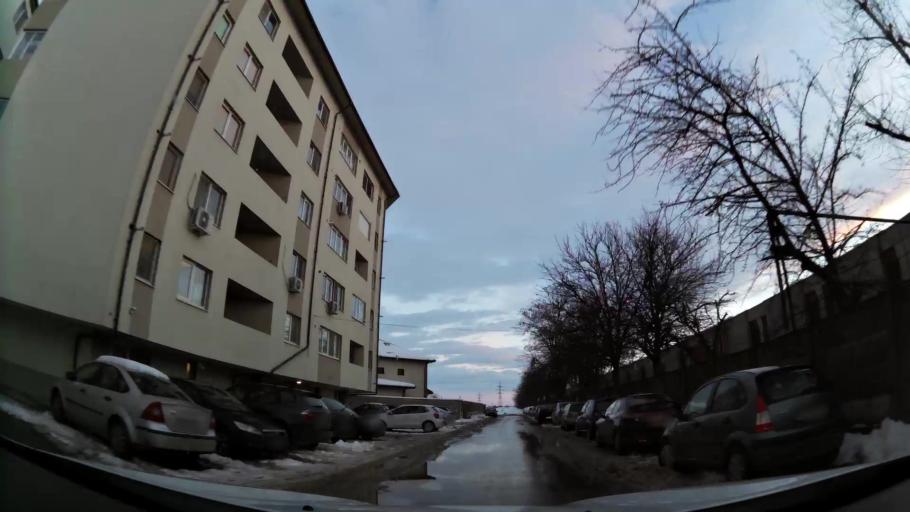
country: RO
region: Ilfov
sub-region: Comuna Popesti-Leordeni
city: Popesti-Leordeni
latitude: 44.3619
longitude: 26.1499
